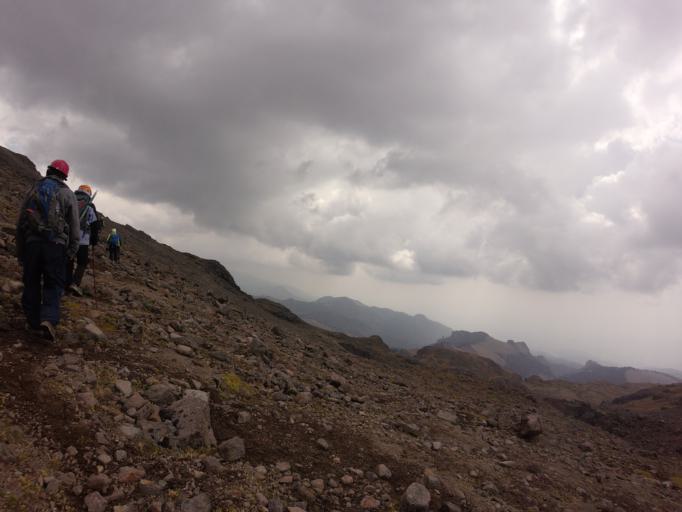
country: MX
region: Mexico
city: Amecameca de Juarez
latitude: 19.1555
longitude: -98.6417
